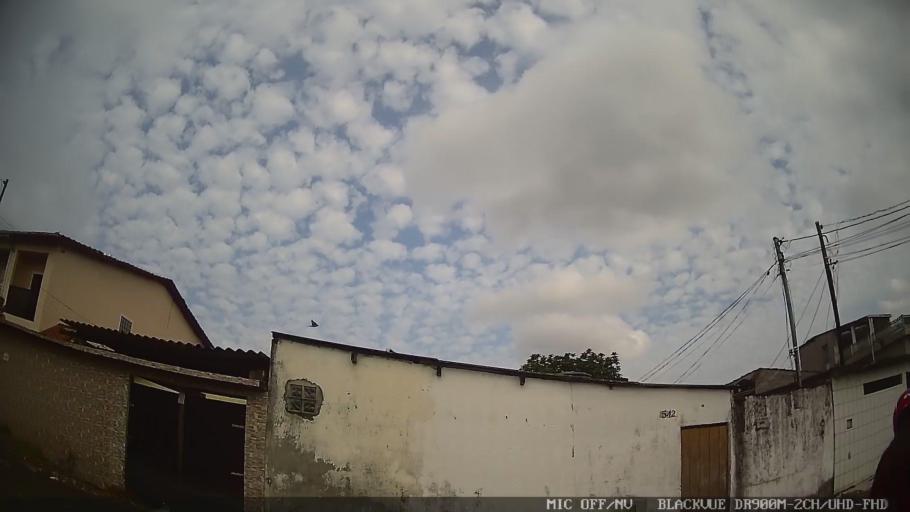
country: BR
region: Sao Paulo
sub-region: Guaruja
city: Guaruja
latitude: -23.9589
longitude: -46.2809
